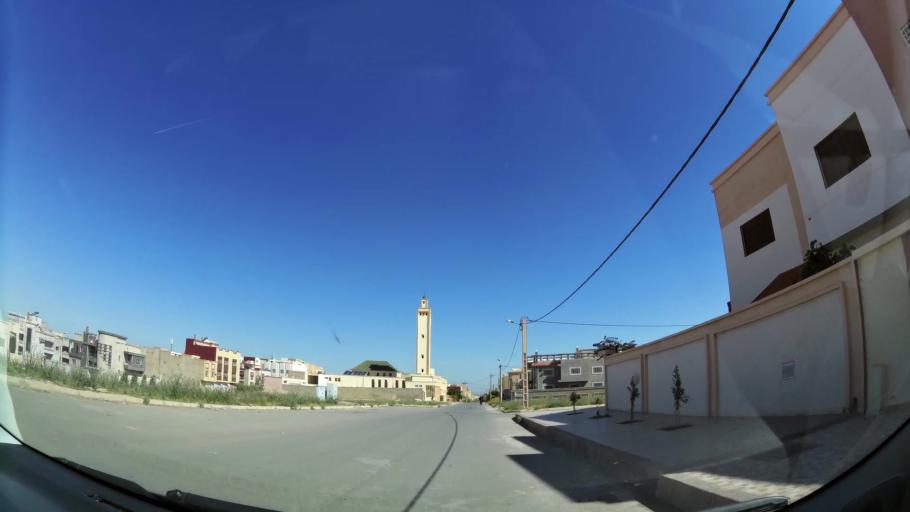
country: MA
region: Oriental
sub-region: Oujda-Angad
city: Oujda
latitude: 34.6539
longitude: -1.8864
